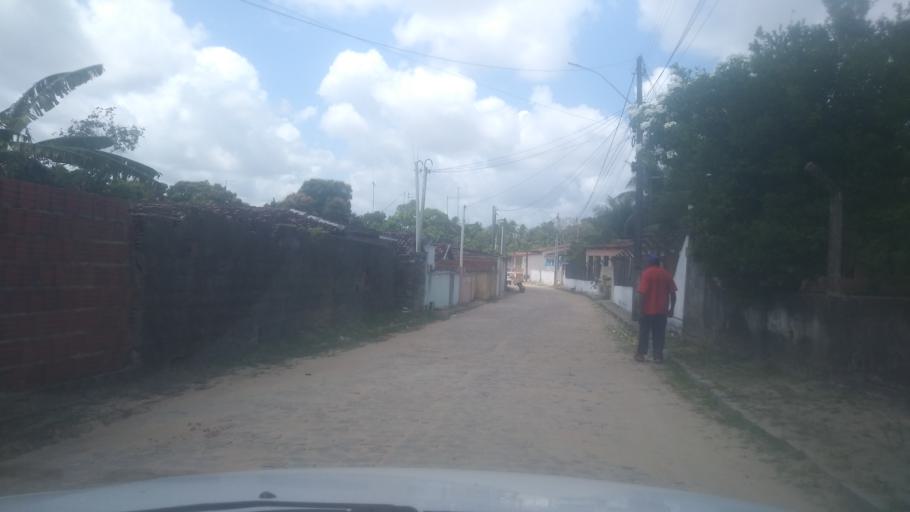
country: BR
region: Rio Grande do Norte
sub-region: Sao Jose De Mipibu
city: Sao Jose de Mipibu
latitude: -6.0697
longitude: -35.2279
